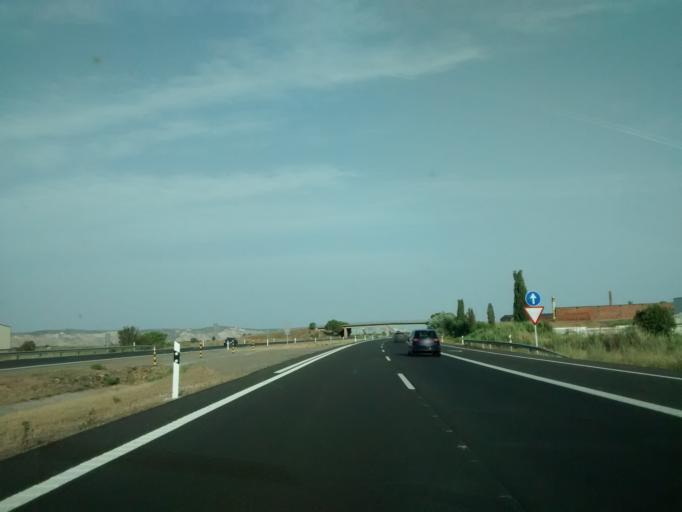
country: ES
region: Aragon
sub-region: Provincia de Zaragoza
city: Alagon
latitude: 41.7761
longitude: -1.1175
